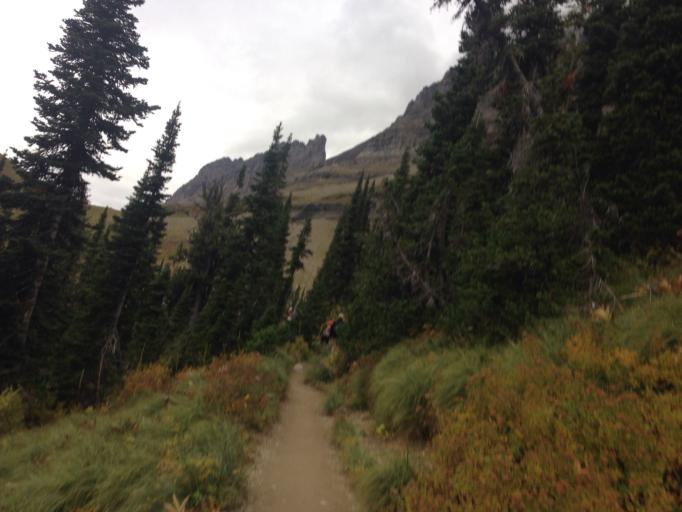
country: US
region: Montana
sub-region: Flathead County
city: Columbia Falls
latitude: 48.7322
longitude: -113.7207
